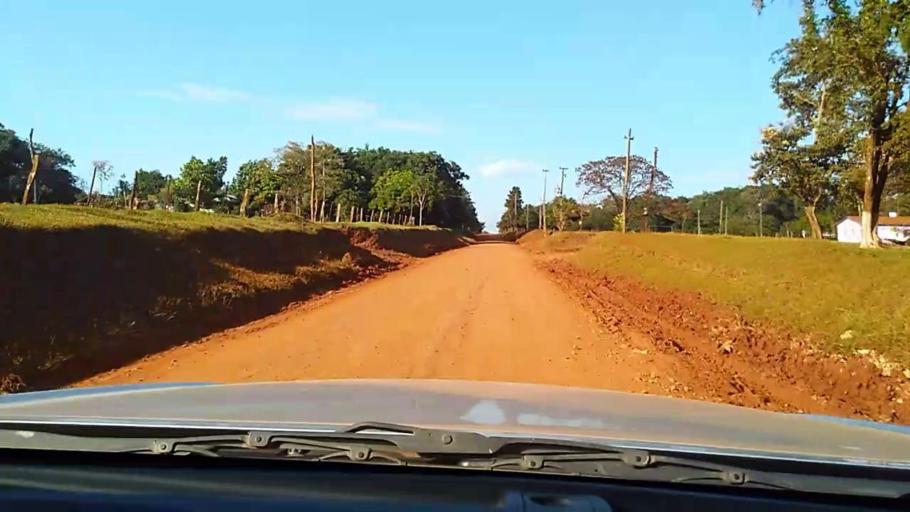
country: PY
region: Alto Parana
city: Doctor Juan Leon Mallorquin
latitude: -25.6890
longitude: -55.3774
